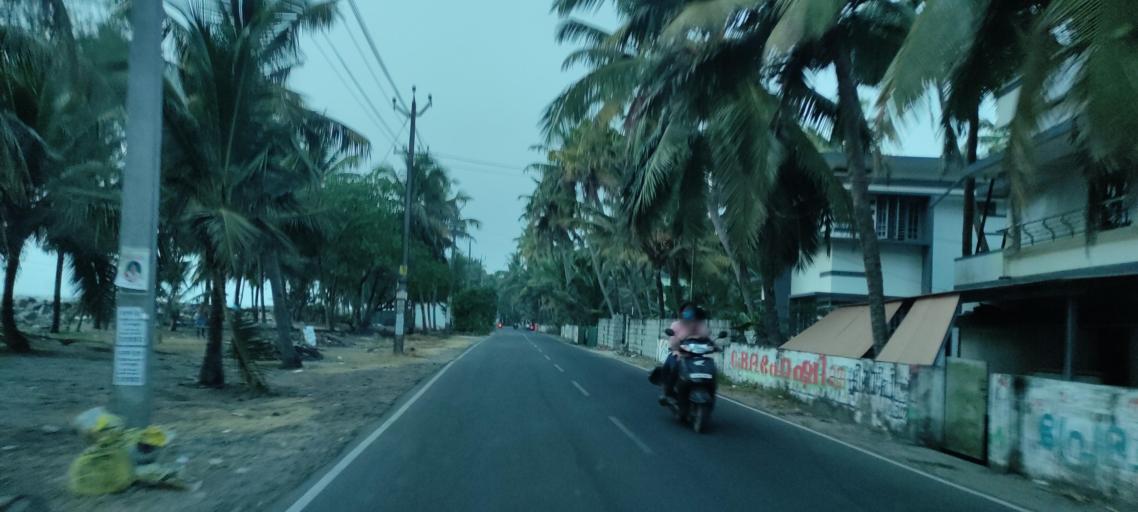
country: IN
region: Kerala
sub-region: Alappuzha
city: Kayankulam
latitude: 9.1183
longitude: 76.4715
